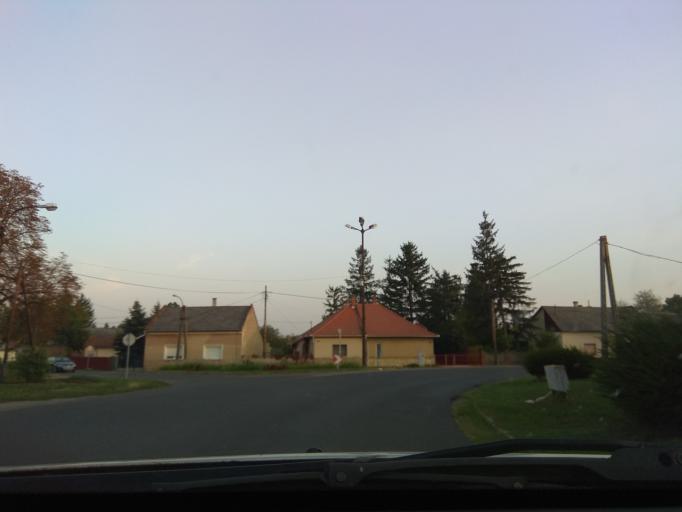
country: HU
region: Borsod-Abauj-Zemplen
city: Szerencs
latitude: 48.1640
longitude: 21.2067
